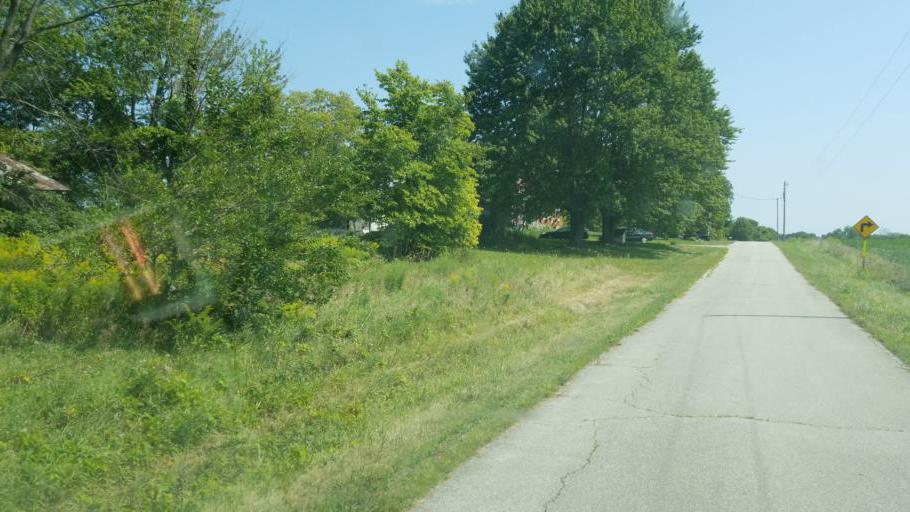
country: US
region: Ohio
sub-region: Crawford County
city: Bucyrus
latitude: 40.8488
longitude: -83.1048
